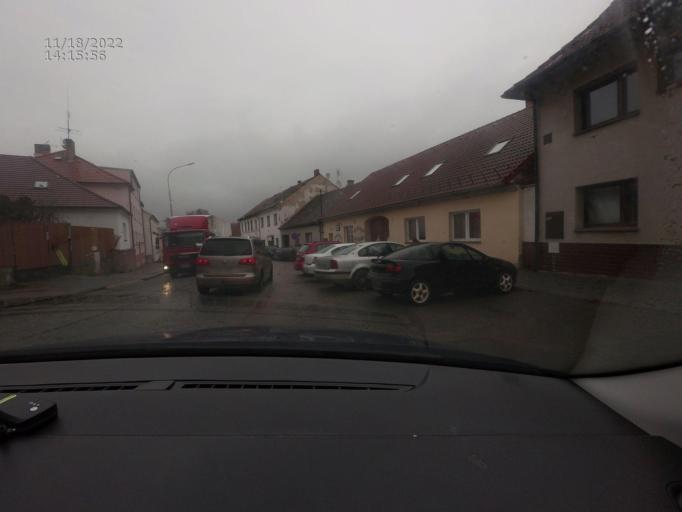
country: CZ
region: Jihocesky
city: Mirotice
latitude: 49.4289
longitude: 14.0371
